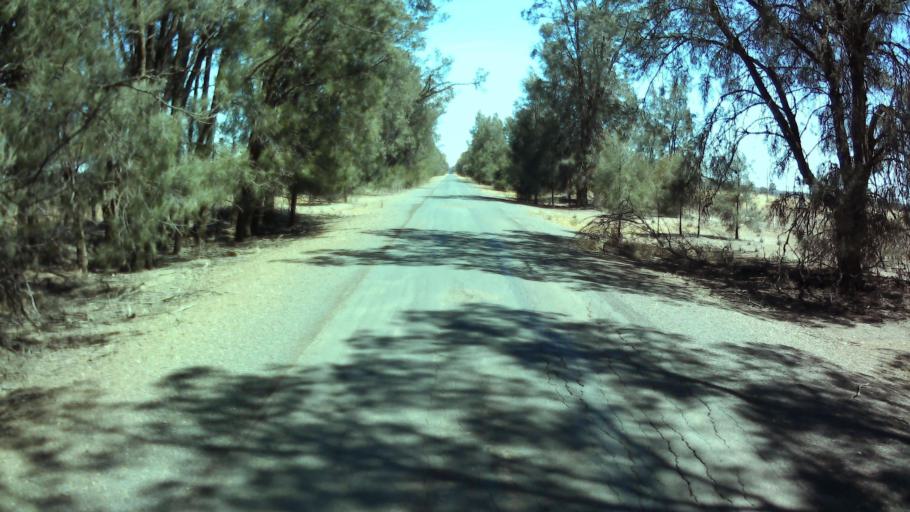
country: AU
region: New South Wales
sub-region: Weddin
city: Grenfell
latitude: -33.8846
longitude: 147.6894
